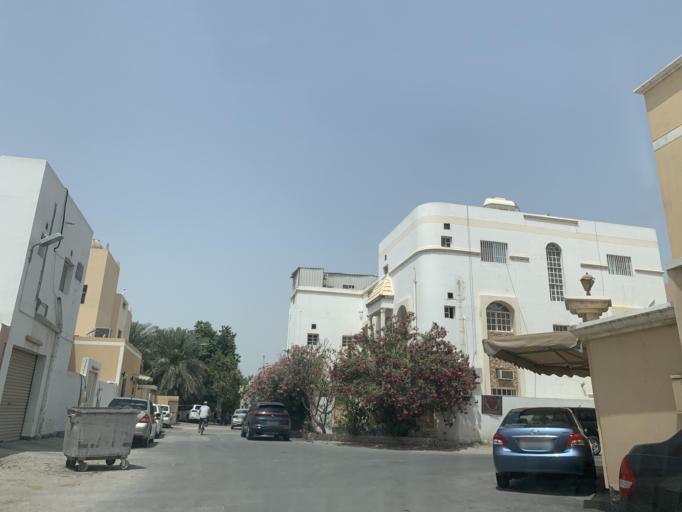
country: BH
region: Northern
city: Madinat `Isa
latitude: 26.1819
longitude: 50.5504
